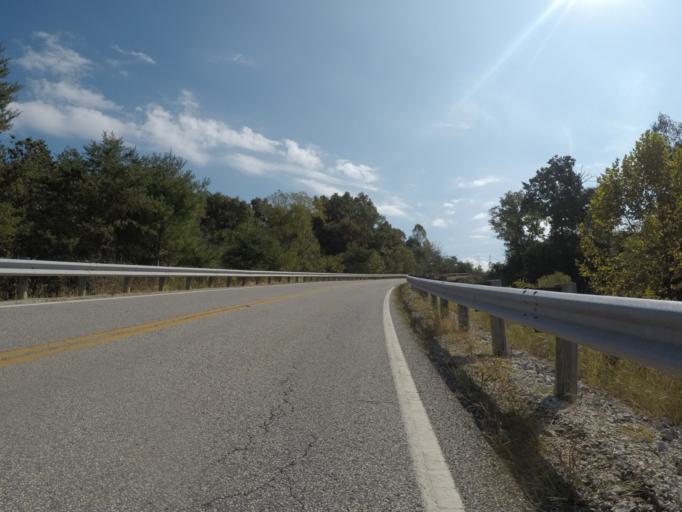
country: US
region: West Virginia
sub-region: Cabell County
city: Lesage
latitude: 38.5911
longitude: -82.4276
